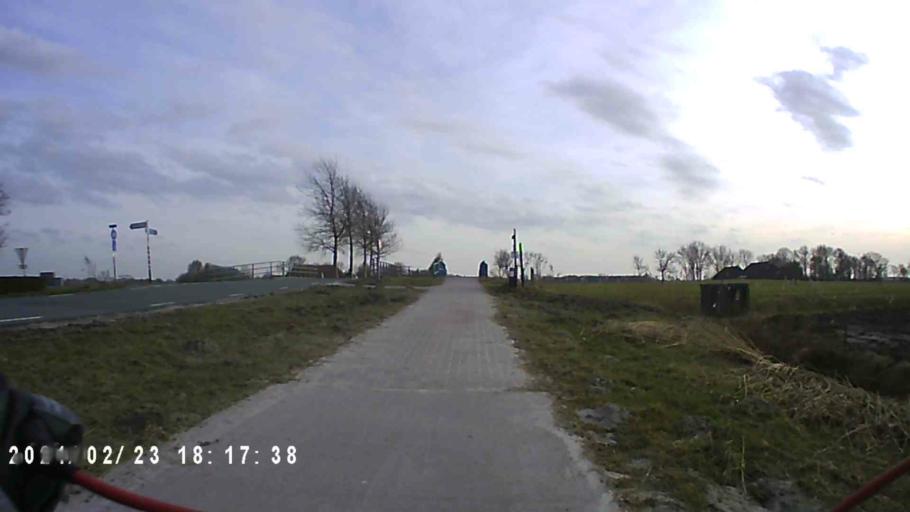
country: NL
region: Groningen
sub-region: Gemeente Bedum
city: Bedum
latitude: 53.3773
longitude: 6.6277
